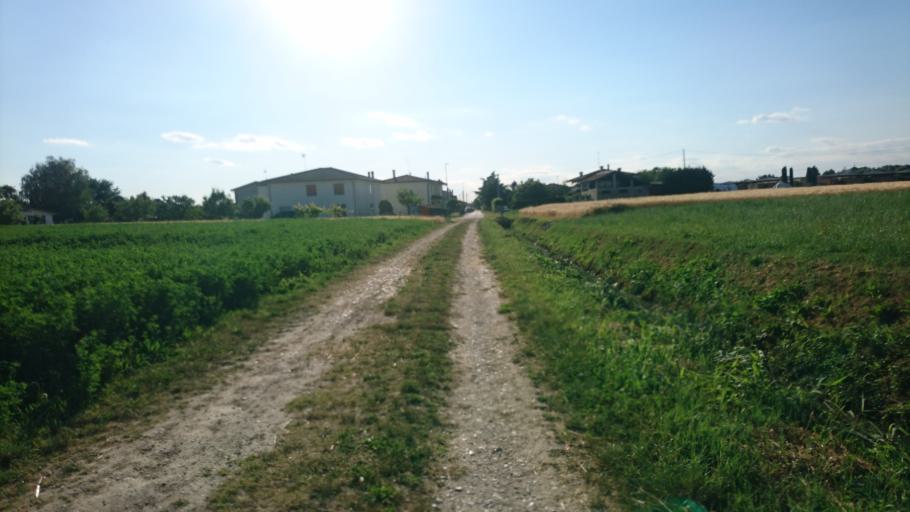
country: IT
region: Veneto
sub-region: Provincia di Padova
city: Ponte San Nicolo
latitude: 45.3639
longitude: 11.9223
